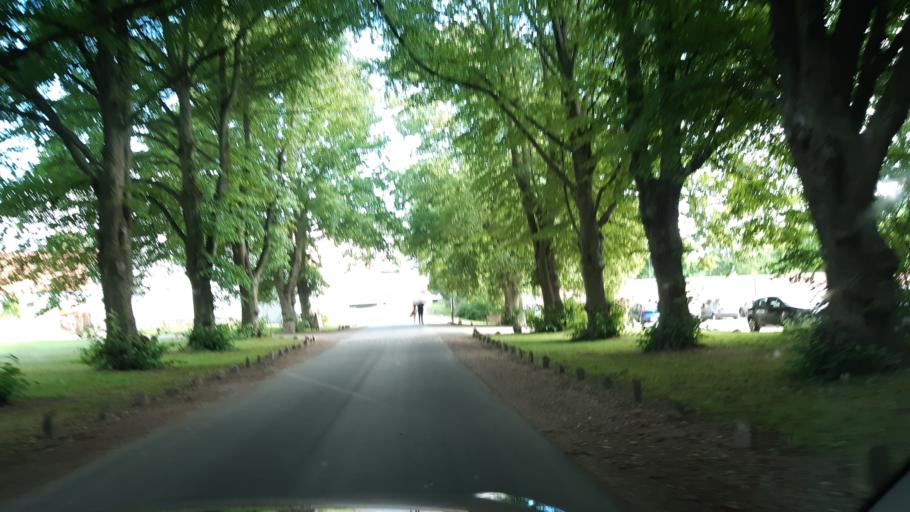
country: DK
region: Zealand
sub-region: Odsherred Kommune
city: Horve
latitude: 55.7732
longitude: 11.3905
